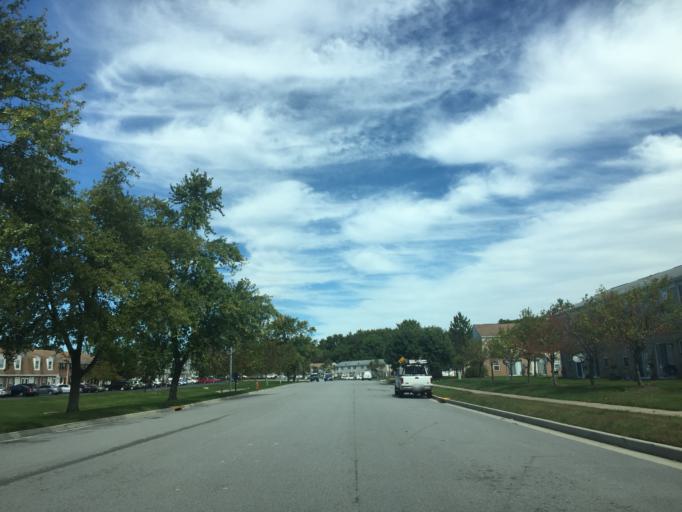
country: US
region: Maryland
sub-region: Baltimore County
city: Middle River
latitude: 39.3480
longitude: -76.4412
